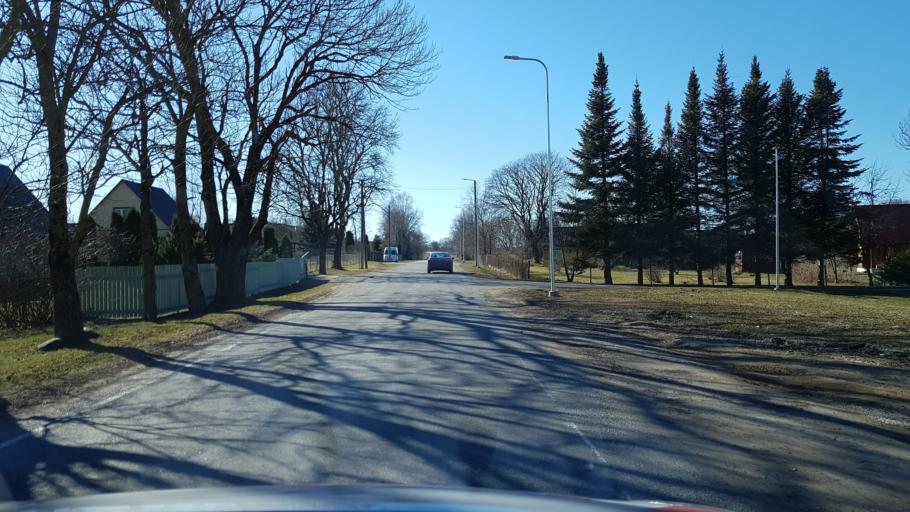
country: EE
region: Laeaene-Virumaa
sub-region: Haljala vald
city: Haljala
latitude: 59.4334
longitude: 26.2611
